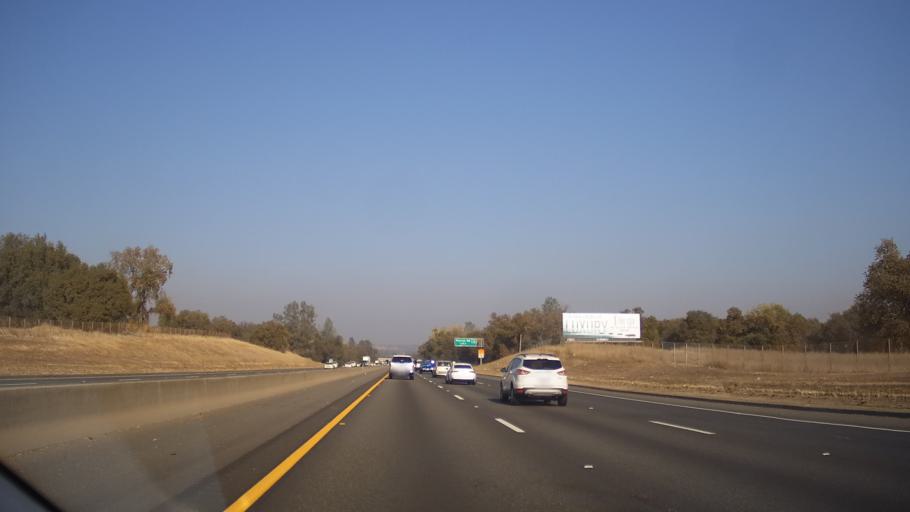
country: US
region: California
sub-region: Placer County
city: Loomis
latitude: 38.8198
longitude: -121.1853
